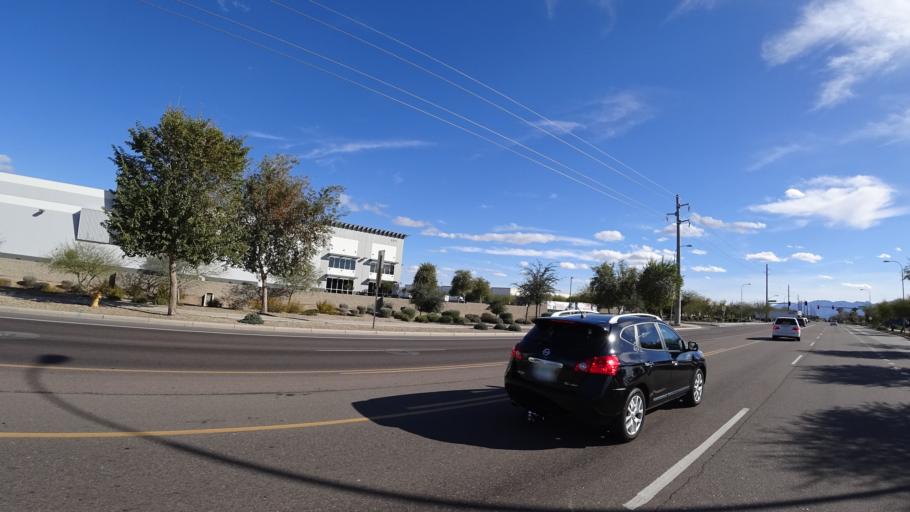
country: US
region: Arizona
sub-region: Maricopa County
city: Tolleson
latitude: 33.4317
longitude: -112.2216
